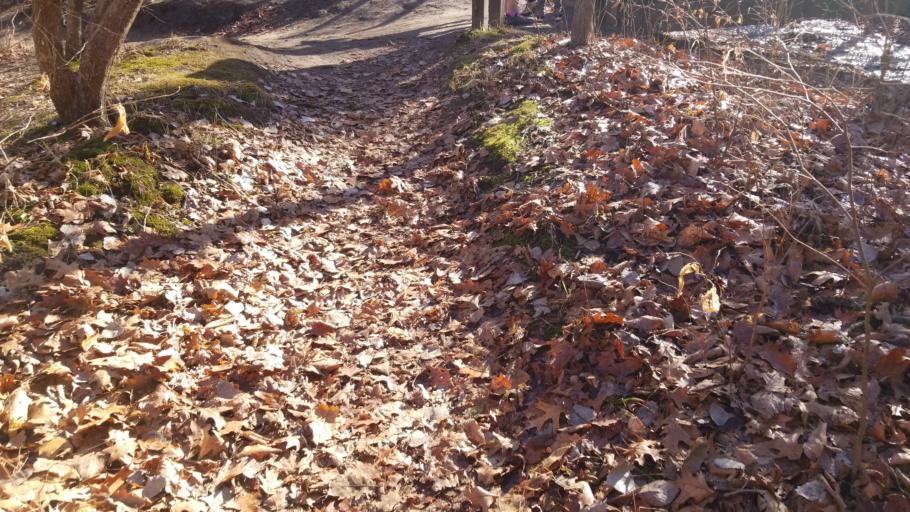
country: US
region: Nebraska
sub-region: Cass County
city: Louisville
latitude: 40.9901
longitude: -96.2179
